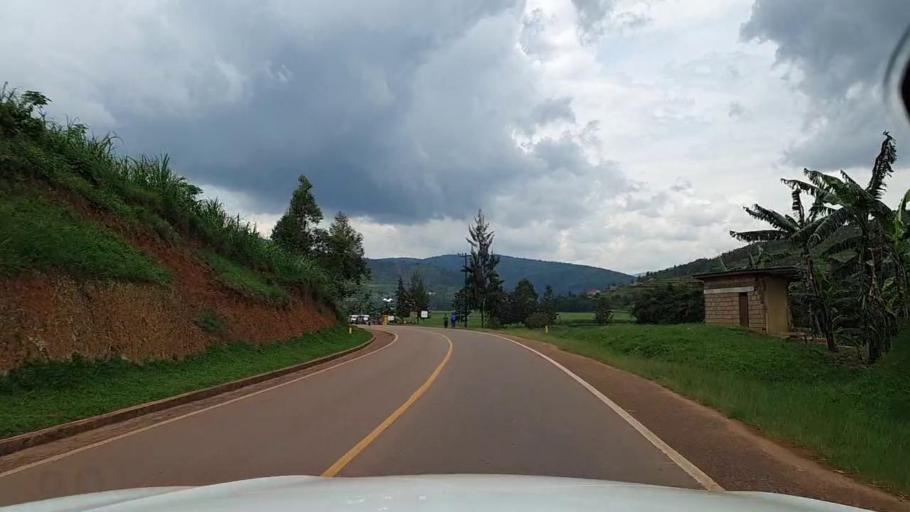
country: RW
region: Kigali
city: Kigali
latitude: -1.7798
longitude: 30.1303
